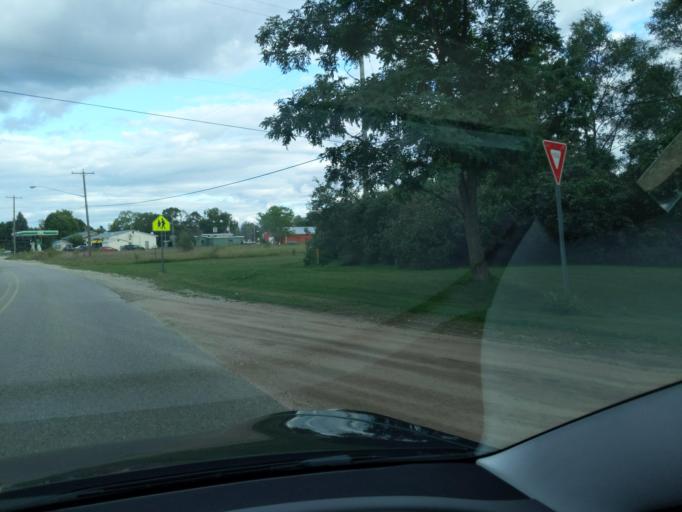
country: US
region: Michigan
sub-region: Kalkaska County
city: Rapid City
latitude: 44.8344
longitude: -85.2850
